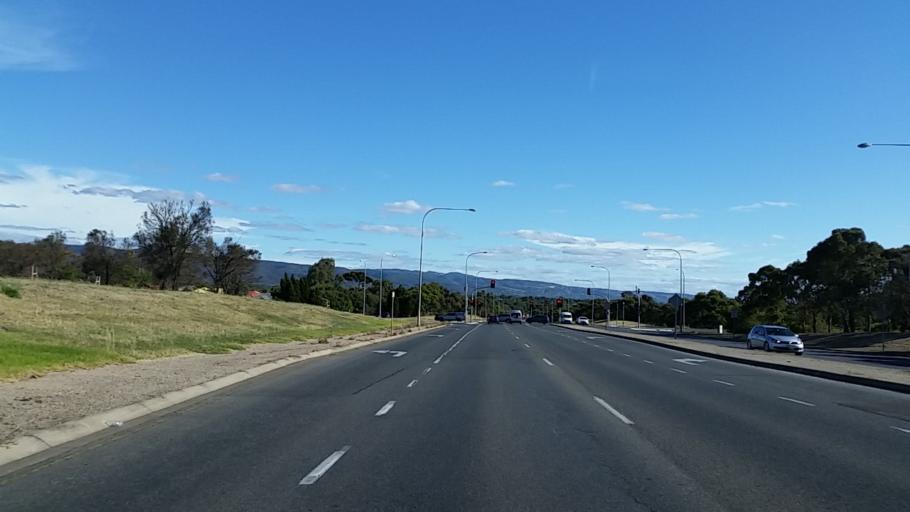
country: AU
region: South Australia
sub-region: Tea Tree Gully
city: Modbury
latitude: -34.8272
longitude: 138.6799
